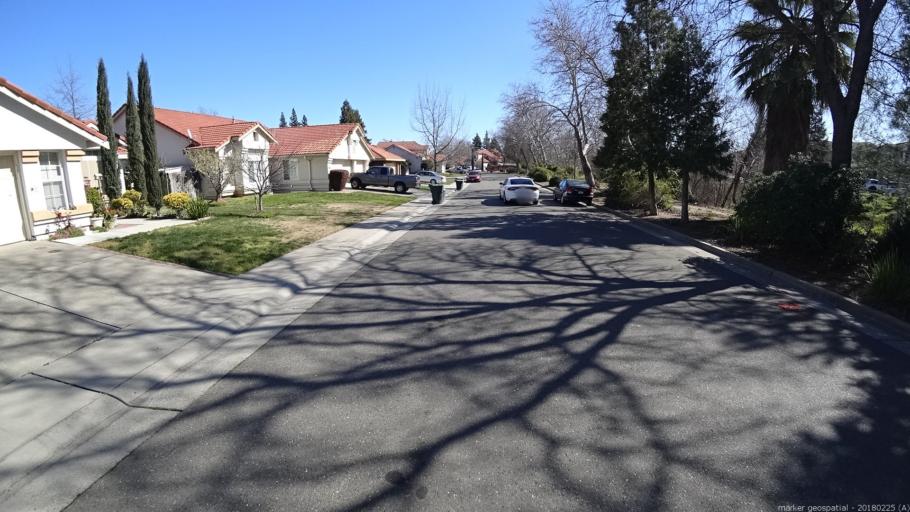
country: US
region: California
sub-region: Sacramento County
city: North Highlands
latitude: 38.7144
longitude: -121.3730
